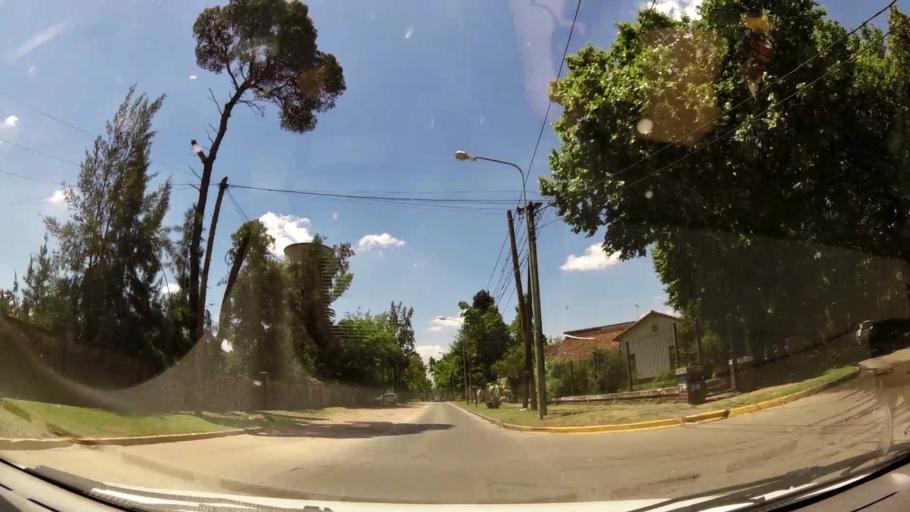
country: AR
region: Buenos Aires
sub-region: Partido de Merlo
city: Merlo
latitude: -34.6628
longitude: -58.7008
